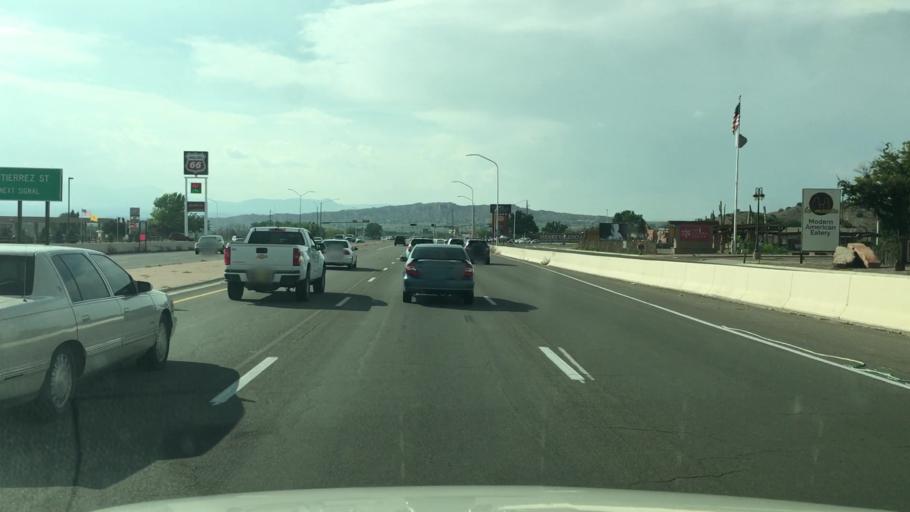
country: US
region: New Mexico
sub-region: Santa Fe County
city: Pojoaque
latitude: 35.8808
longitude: -106.0121
